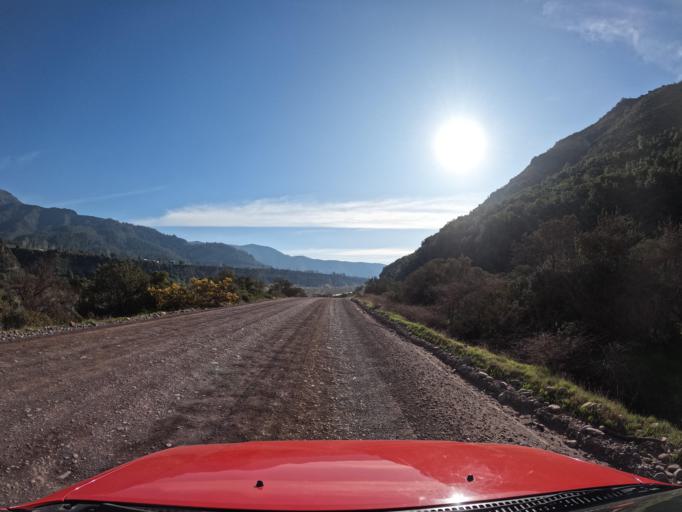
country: CL
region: Maule
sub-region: Provincia de Curico
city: Teno
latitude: -35.0019
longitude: -70.8350
